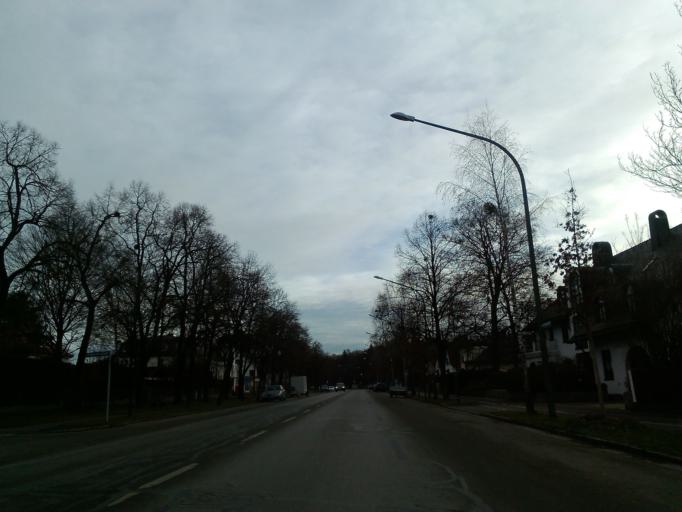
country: DE
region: Bavaria
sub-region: Upper Bavaria
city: Neuried
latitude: 48.1128
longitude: 11.4915
